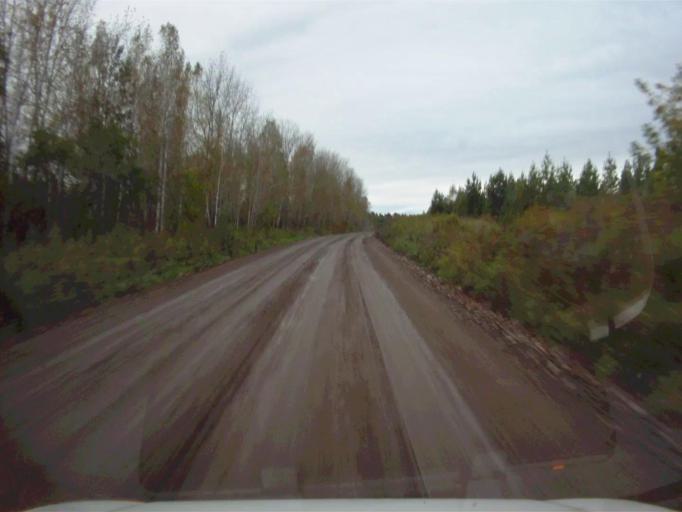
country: RU
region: Chelyabinsk
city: Nyazepetrovsk
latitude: 56.1366
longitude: 59.3015
